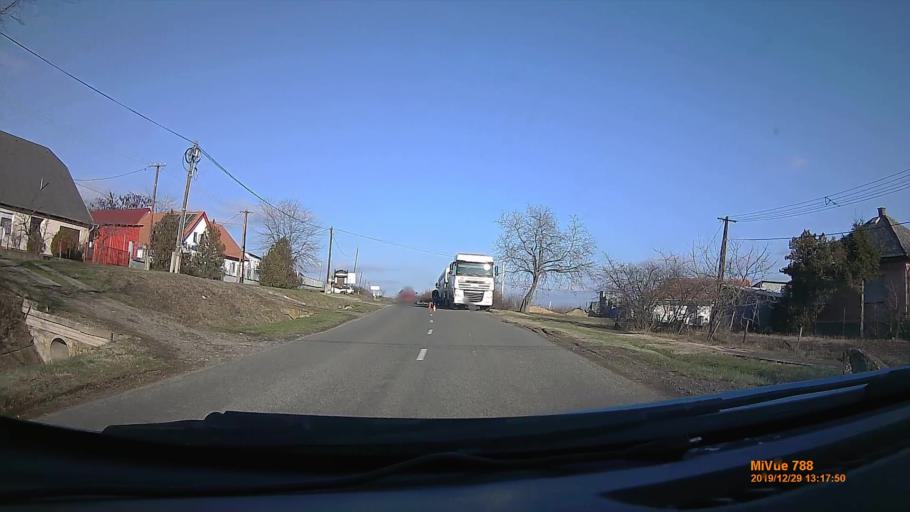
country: HU
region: Heves
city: Domoszlo
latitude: 47.8318
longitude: 20.1264
